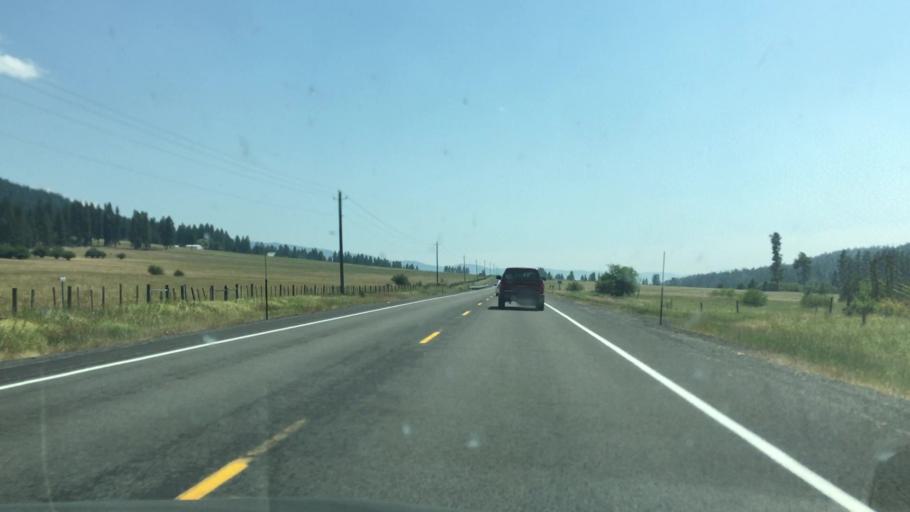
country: US
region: Idaho
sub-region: Valley County
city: McCall
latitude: 45.0735
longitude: -116.2965
